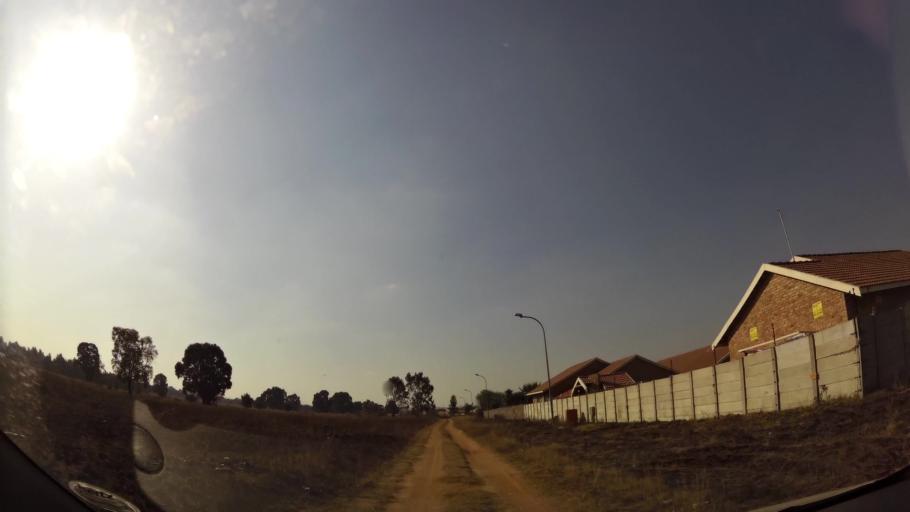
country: ZA
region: Gauteng
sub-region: West Rand District Municipality
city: Randfontein
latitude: -26.1827
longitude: 27.6773
